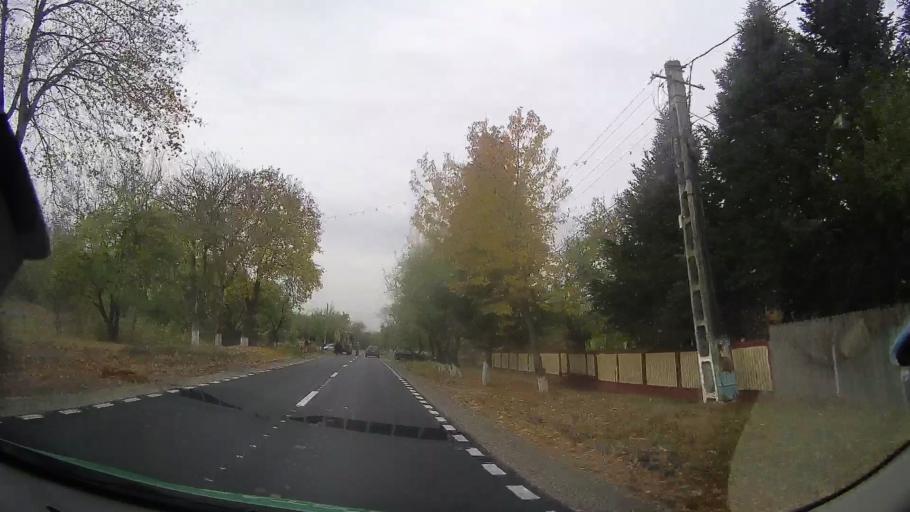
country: RO
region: Ilfov
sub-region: Comuna Nuci
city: Nuci
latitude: 44.7192
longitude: 26.3066
